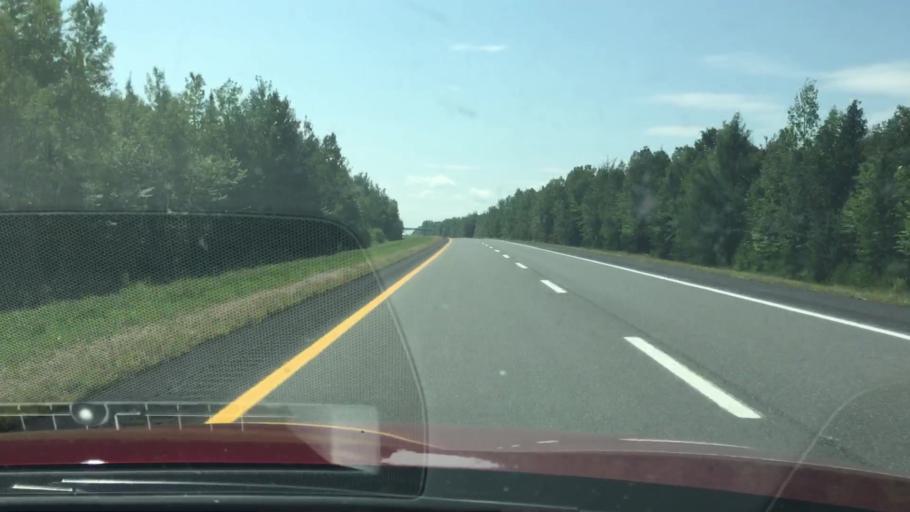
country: US
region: Maine
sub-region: Penobscot County
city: Patten
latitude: 45.9536
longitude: -68.3310
